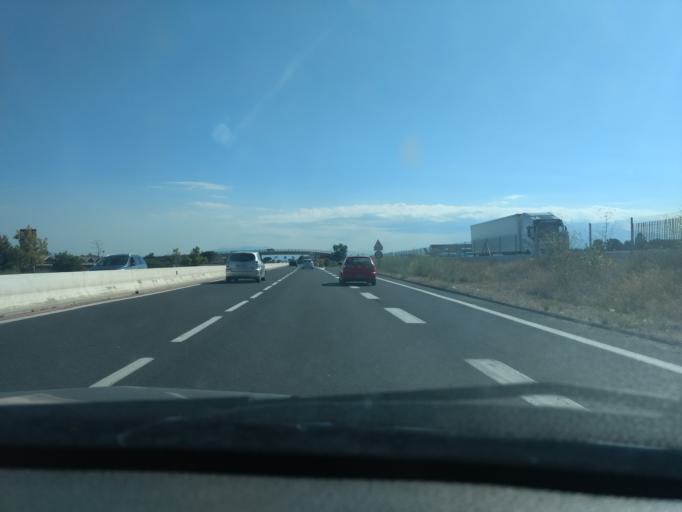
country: FR
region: Languedoc-Roussillon
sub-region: Departement des Pyrenees-Orientales
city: Pia
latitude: 42.7374
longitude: 2.8857
